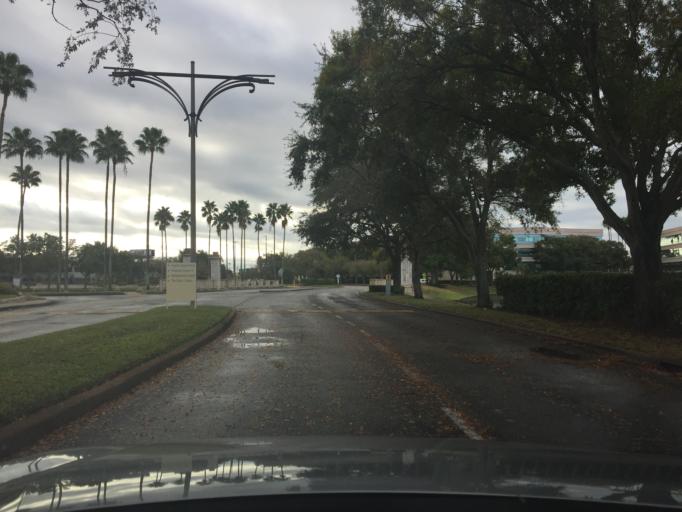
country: US
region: Florida
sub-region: Hillsborough County
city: Town 'n' Country
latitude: 27.9802
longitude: -82.5490
